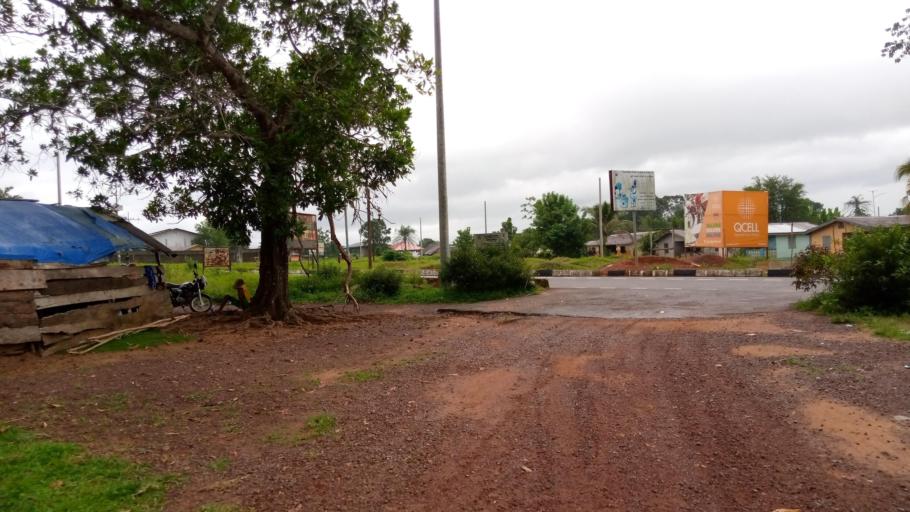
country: SL
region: Southern Province
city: Moyamba
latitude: 8.1611
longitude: -12.4377
